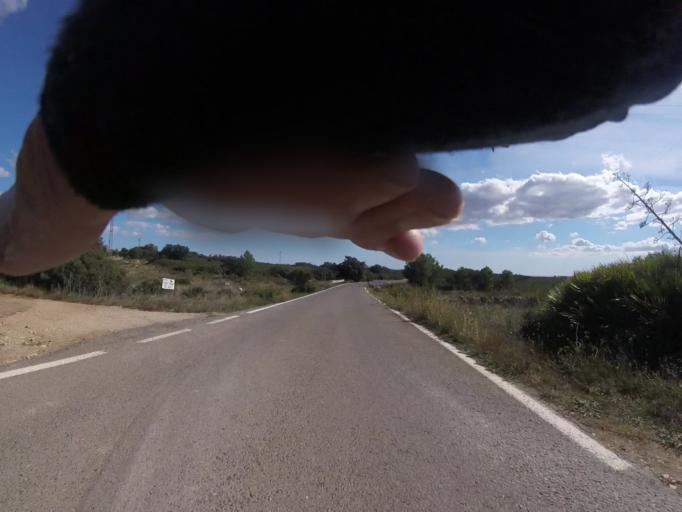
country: ES
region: Valencia
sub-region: Provincia de Castello
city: Albocasser
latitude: 40.3990
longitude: 0.0866
